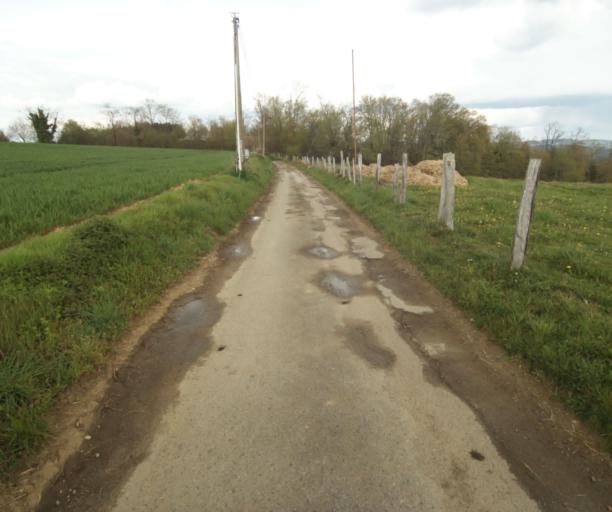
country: FR
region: Limousin
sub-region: Departement de la Correze
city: Tulle
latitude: 45.2807
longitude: 1.7474
